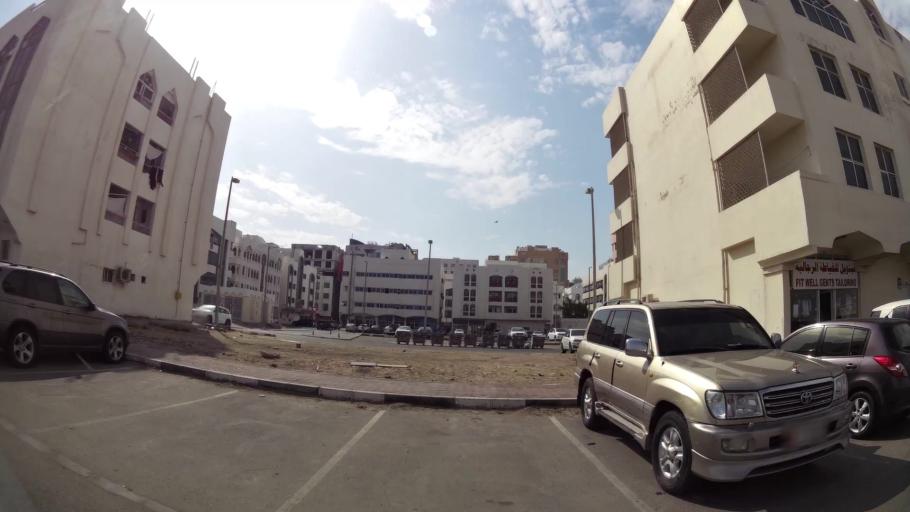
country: AE
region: Abu Dhabi
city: Abu Dhabi
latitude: 24.3281
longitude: 54.5387
